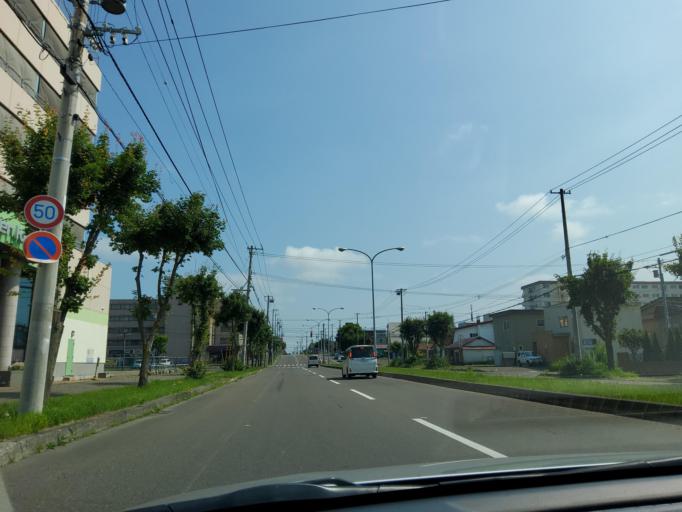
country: JP
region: Hokkaido
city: Obihiro
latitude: 42.9193
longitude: 143.1929
